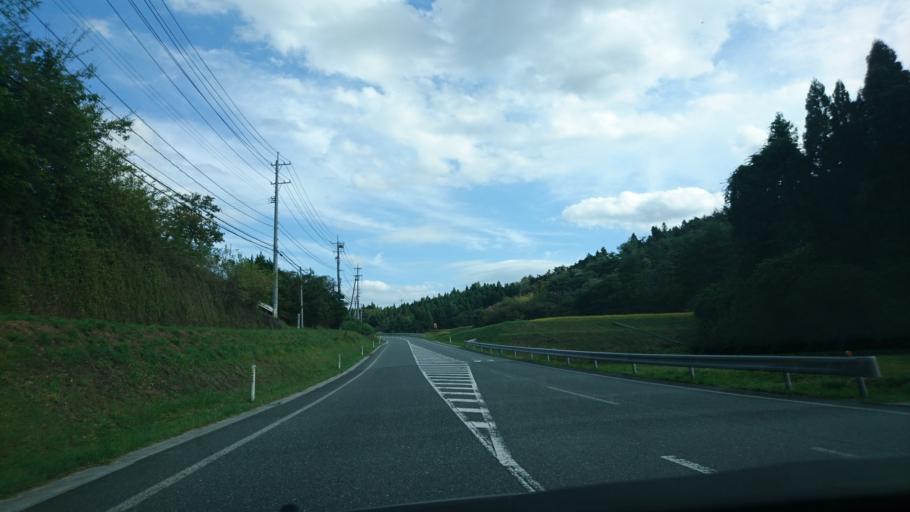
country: JP
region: Iwate
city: Ichinoseki
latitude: 38.8329
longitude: 141.2181
